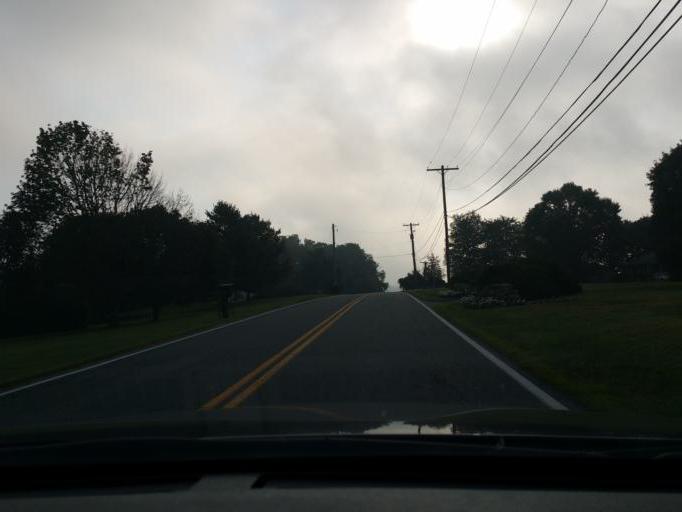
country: US
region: Maryland
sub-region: Cecil County
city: Rising Sun
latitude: 39.6712
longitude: -76.1131
